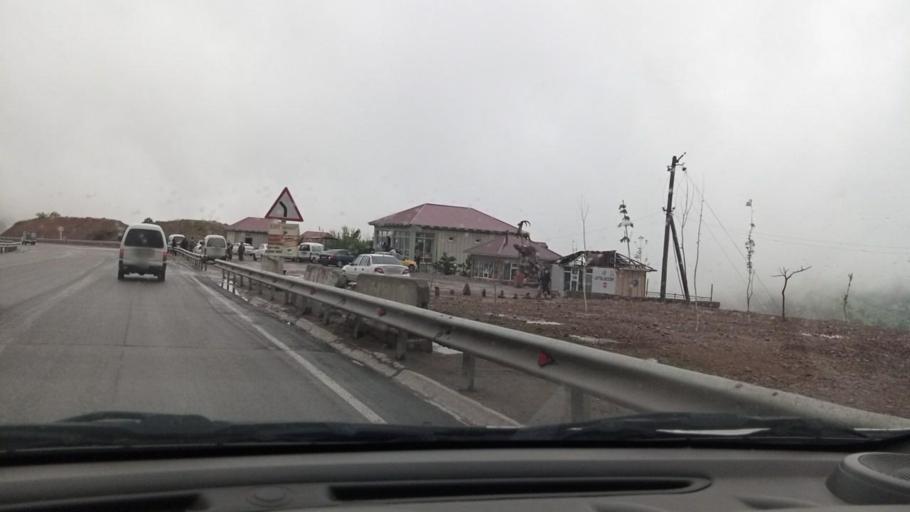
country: UZ
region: Toshkent
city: Angren
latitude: 41.1121
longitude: 70.5041
